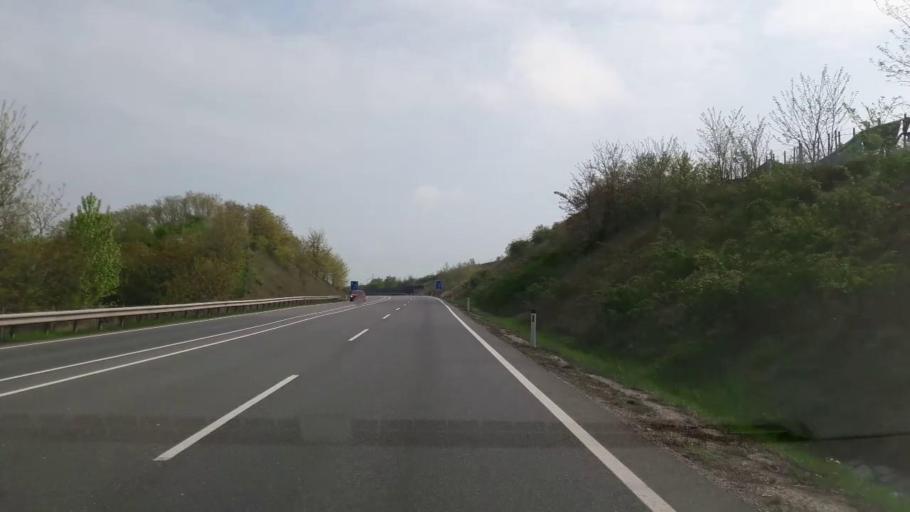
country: AT
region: Lower Austria
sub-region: Politischer Bezirk Hollabrunn
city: Haugsdorf
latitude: 48.7317
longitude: 16.0551
